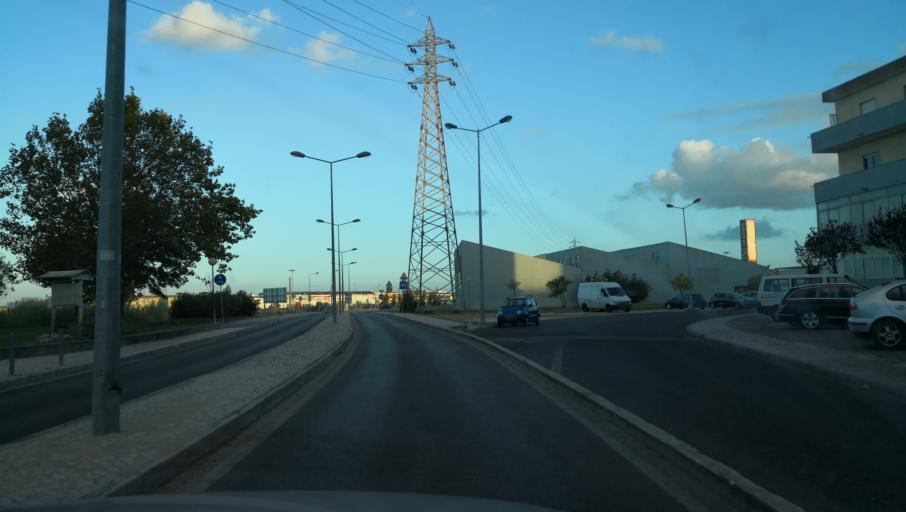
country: PT
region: Setubal
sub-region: Moita
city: Alhos Vedros
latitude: 38.6591
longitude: -9.0405
